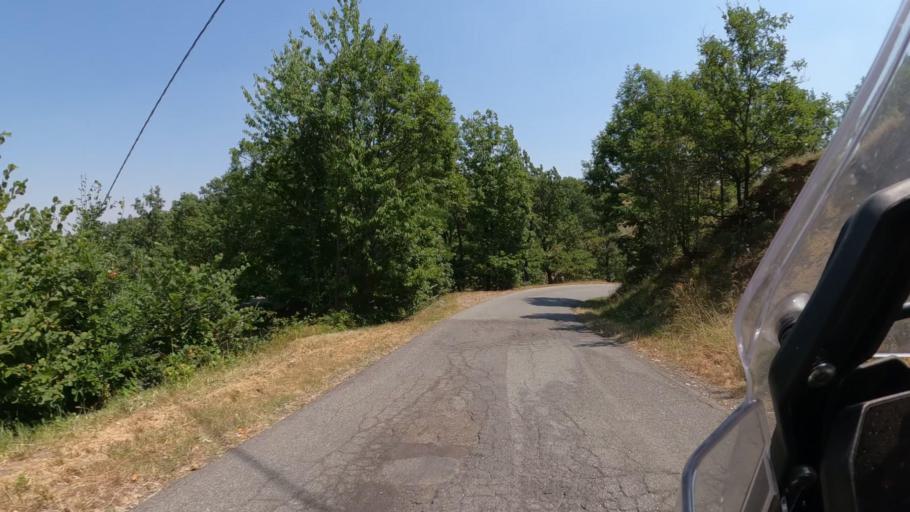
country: IT
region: Piedmont
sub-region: Provincia di Alessandria
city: Cassinelle-Concentrico
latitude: 44.5793
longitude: 8.5406
